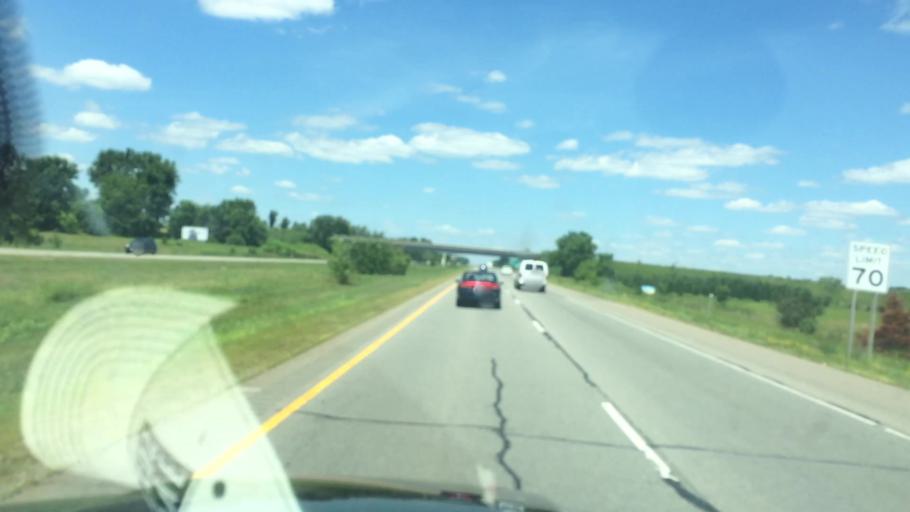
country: US
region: Wisconsin
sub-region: Marathon County
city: Mosinee
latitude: 44.7398
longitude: -89.6796
